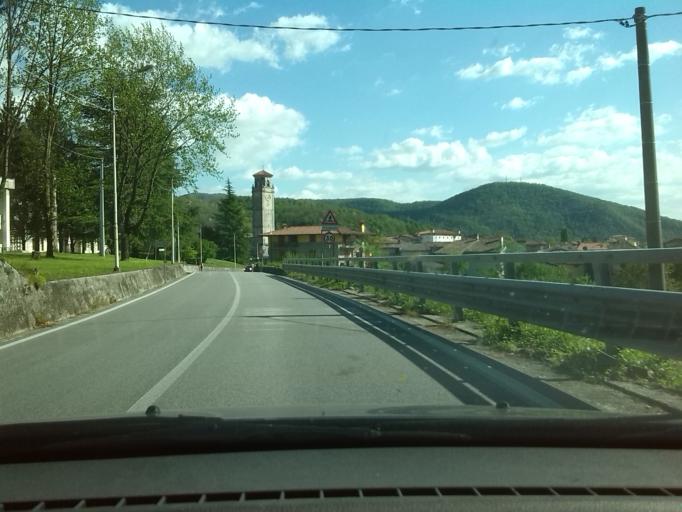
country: IT
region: Friuli Venezia Giulia
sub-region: Provincia di Udine
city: San Pietro al Natisone
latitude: 46.1312
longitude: 13.4856
